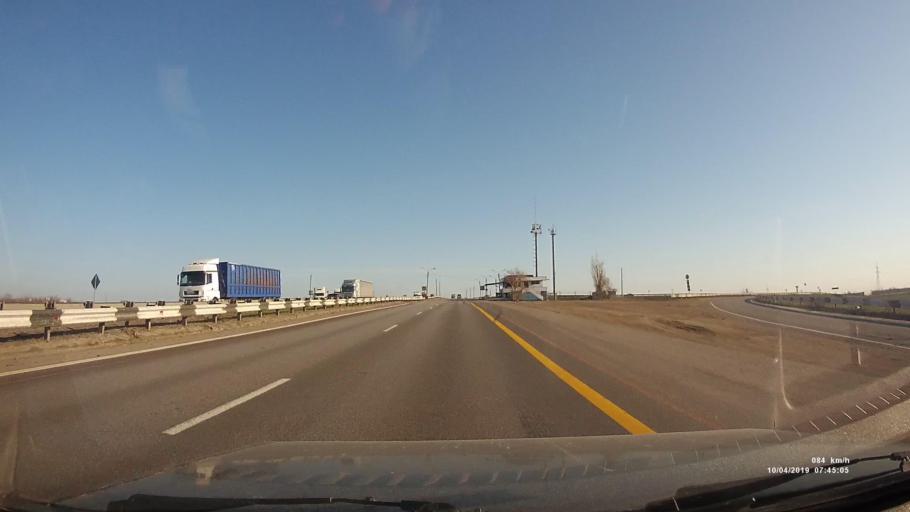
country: RU
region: Rostov
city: Likhoy
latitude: 48.1869
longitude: 40.2660
